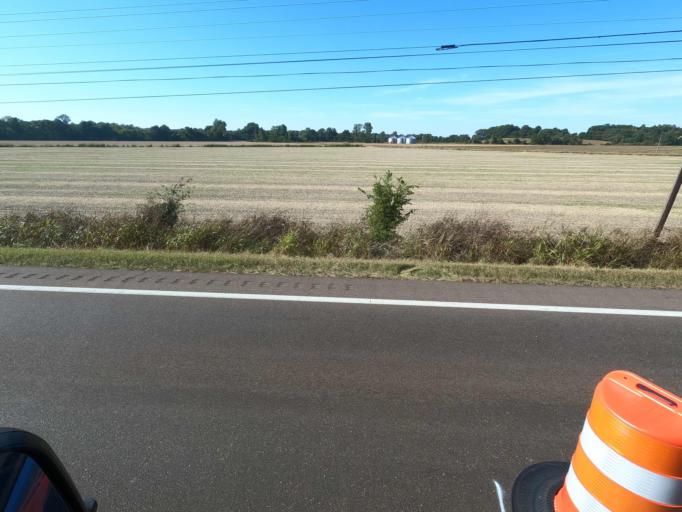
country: US
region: Tennessee
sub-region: Obion County
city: Englewood
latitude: 36.3671
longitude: -89.1266
